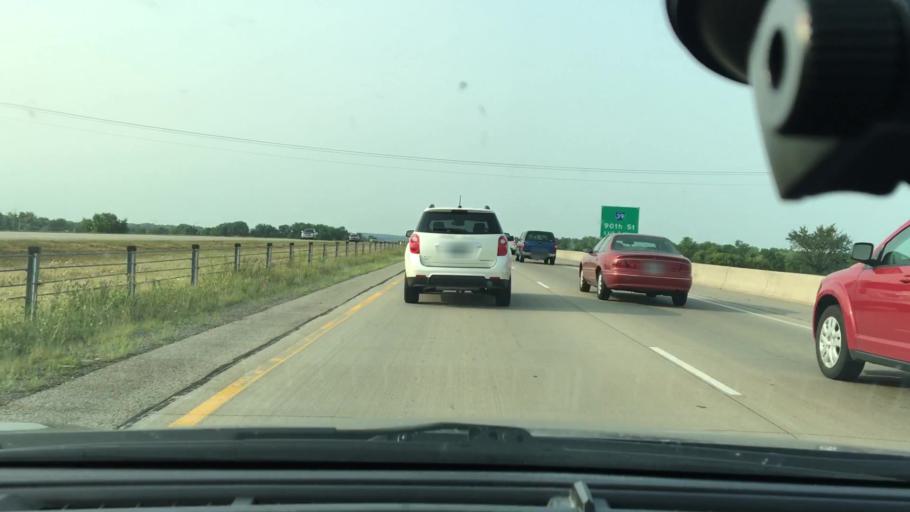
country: US
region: Minnesota
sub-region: Wright County
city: Otsego
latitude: 45.2611
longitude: -93.5556
